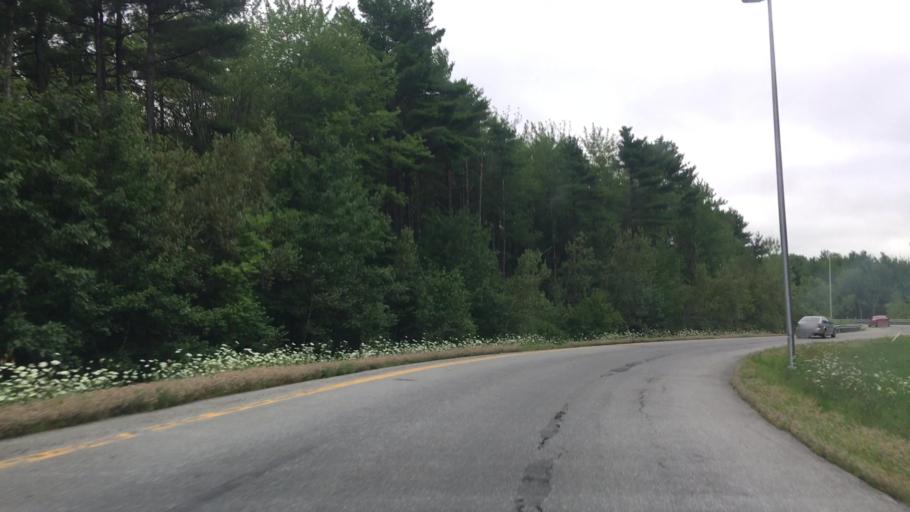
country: US
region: Maine
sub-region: Penobscot County
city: Brewer
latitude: 44.8241
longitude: -68.7566
